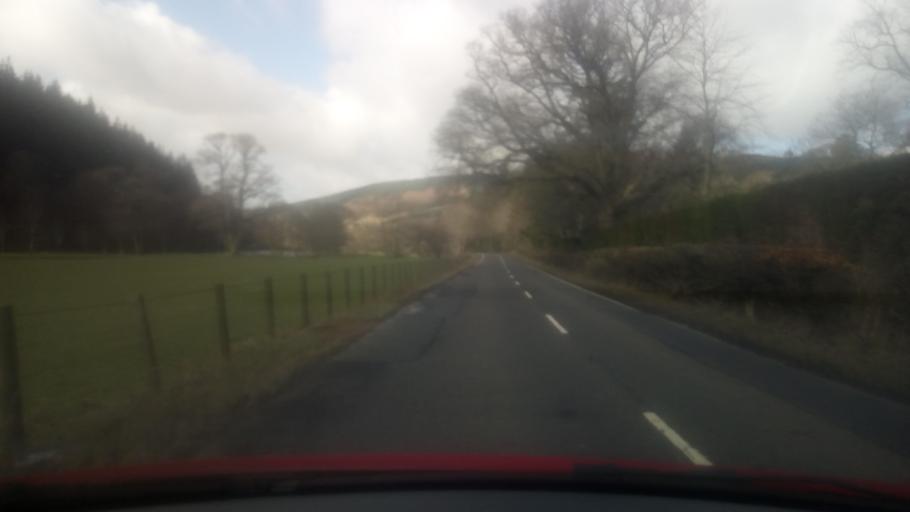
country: GB
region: Scotland
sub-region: The Scottish Borders
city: Innerleithen
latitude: 55.6272
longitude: -2.9722
